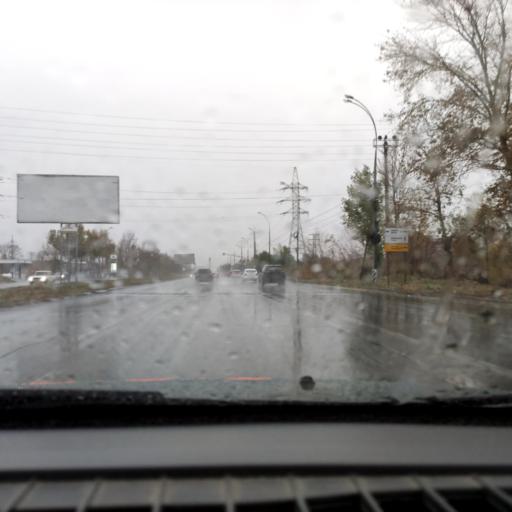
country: RU
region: Samara
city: Tol'yatti
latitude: 53.5447
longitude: 49.2856
